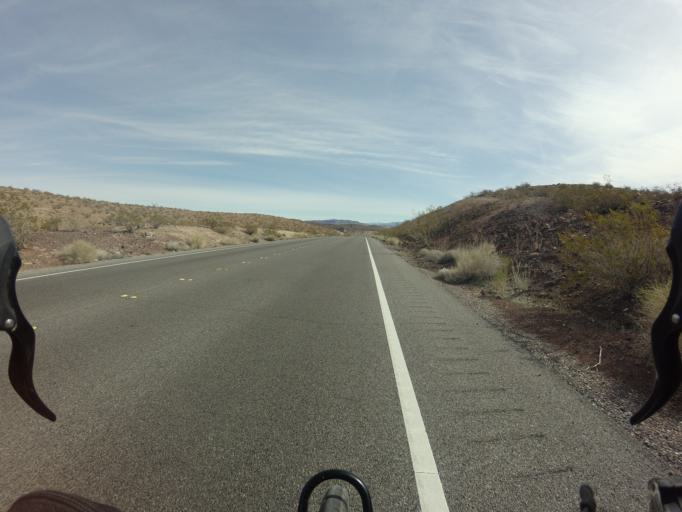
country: US
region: Nevada
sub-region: Clark County
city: Henderson
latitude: 36.1457
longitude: -114.8791
